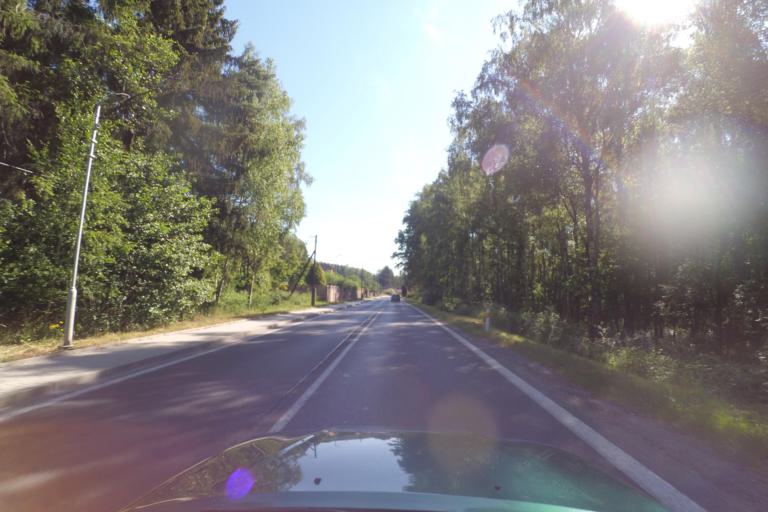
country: CZ
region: Karlovarsky
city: Chodov
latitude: 50.2385
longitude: 12.7709
